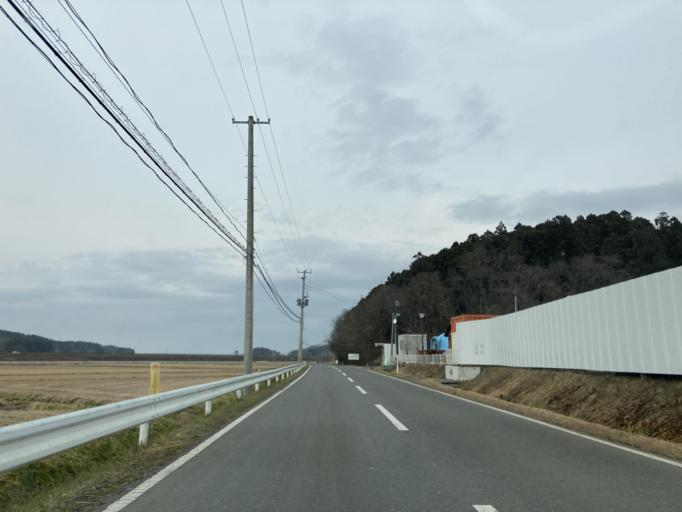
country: JP
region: Miyagi
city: Wakuya
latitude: 38.6838
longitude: 141.2748
